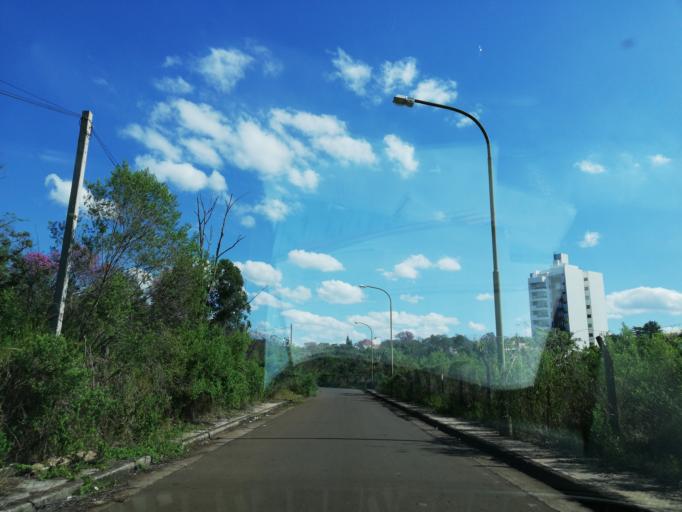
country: AR
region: Misiones
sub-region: Departamento de Capital
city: Posadas
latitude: -27.3605
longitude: -55.9101
